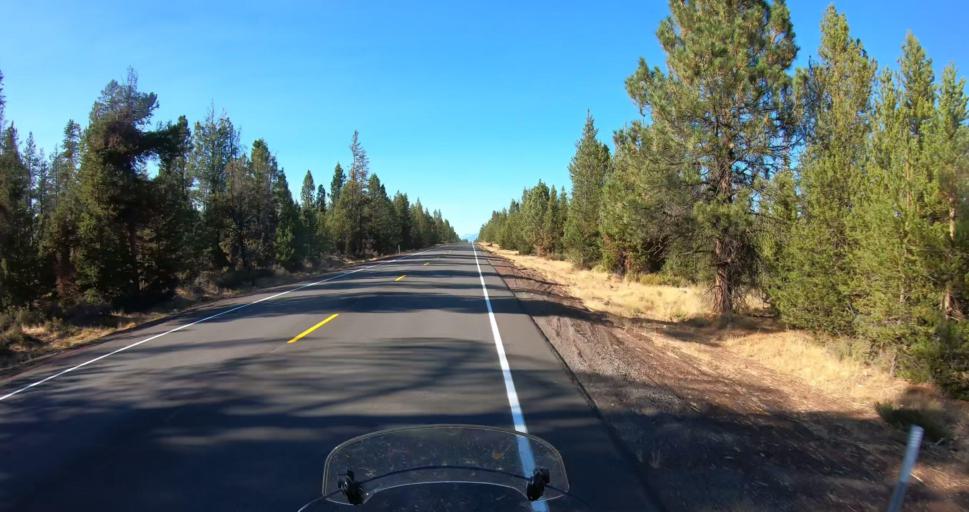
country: US
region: Oregon
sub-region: Deschutes County
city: La Pine
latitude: 43.5403
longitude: -121.4661
